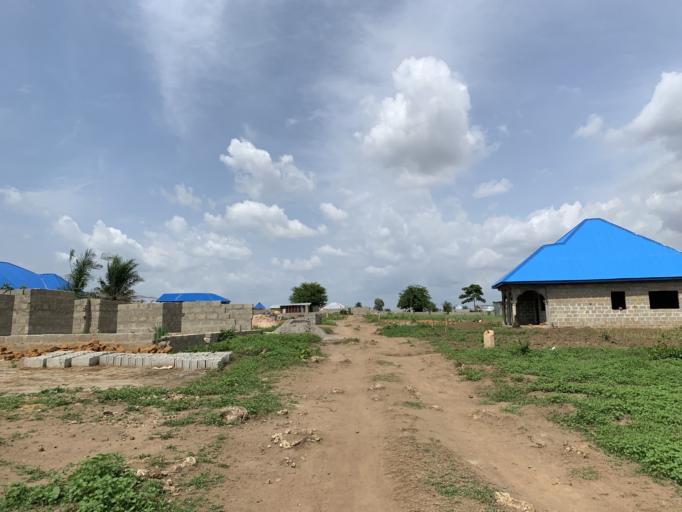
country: SL
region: Western Area
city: Waterloo
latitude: 8.3532
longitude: -13.0474
